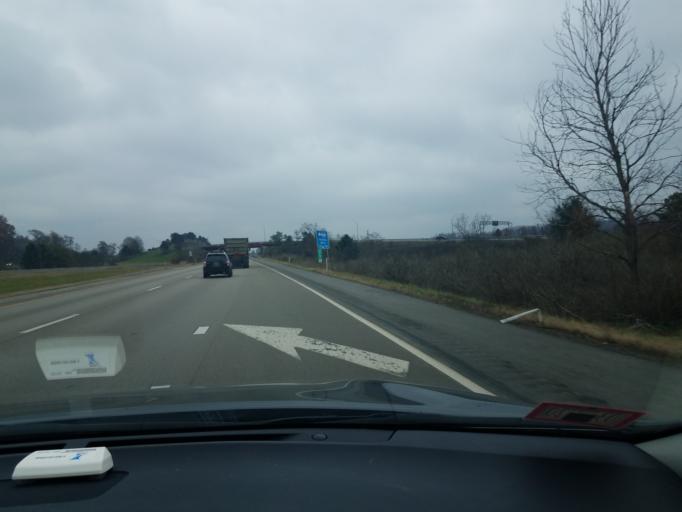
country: US
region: Pennsylvania
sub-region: Butler County
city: Cranberry Township
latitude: 40.6682
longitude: -80.0938
